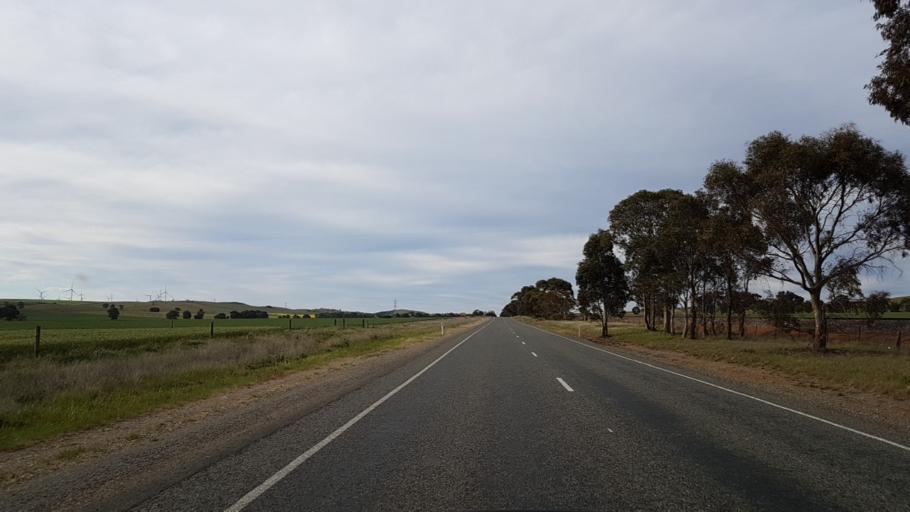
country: AU
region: South Australia
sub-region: Northern Areas
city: Jamestown
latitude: -33.1743
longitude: 138.6121
